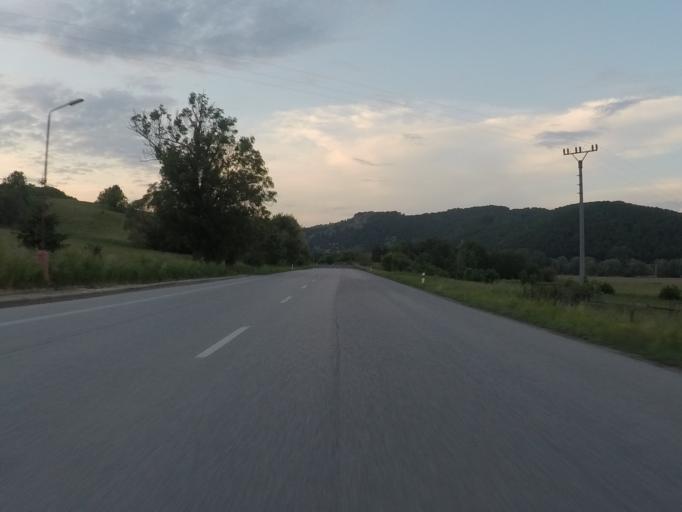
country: SK
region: Banskobystricky
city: Rimavska Sobota
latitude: 48.4813
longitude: 19.9445
